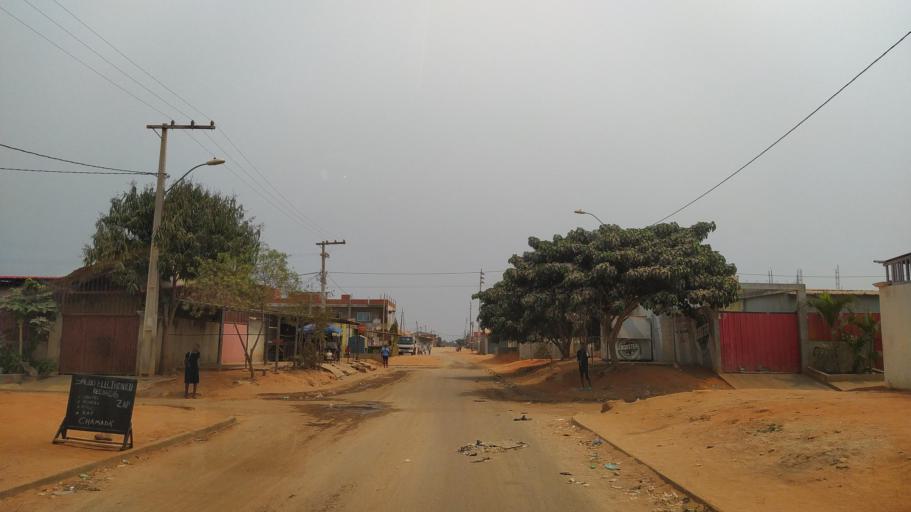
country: AO
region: Luanda
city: Luanda
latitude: -9.0733
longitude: 13.4033
